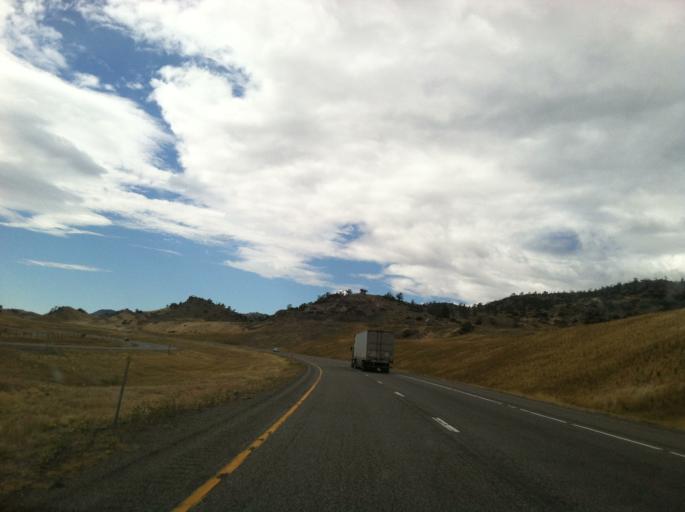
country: US
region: Montana
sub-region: Park County
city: Livingston
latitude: 45.6617
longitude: -110.6407
